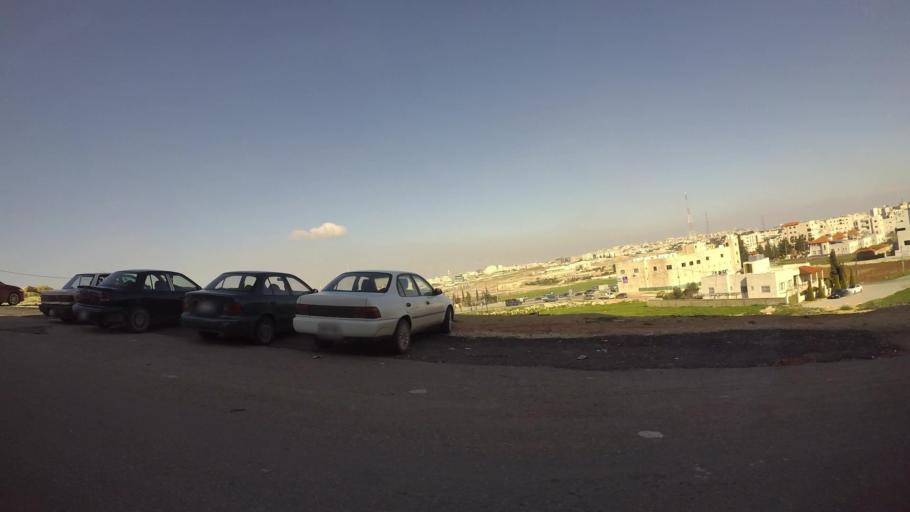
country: JO
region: Amman
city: Al Bunayyat ash Shamaliyah
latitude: 31.9040
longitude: 35.9186
